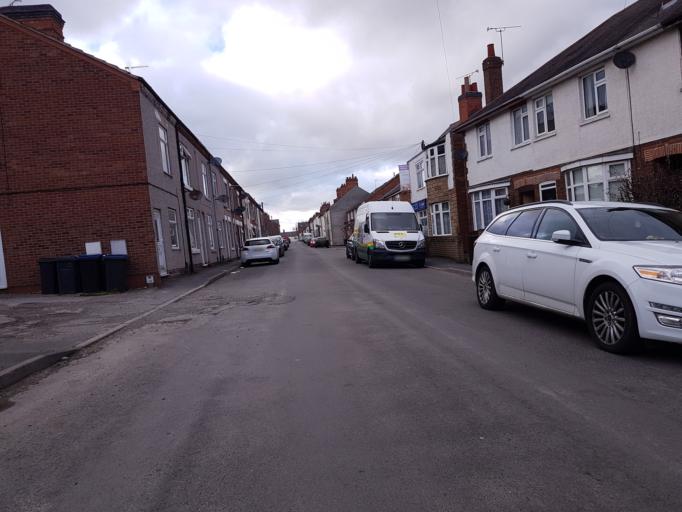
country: GB
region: England
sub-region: Leicestershire
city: Earl Shilton
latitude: 52.5712
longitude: -1.3185
